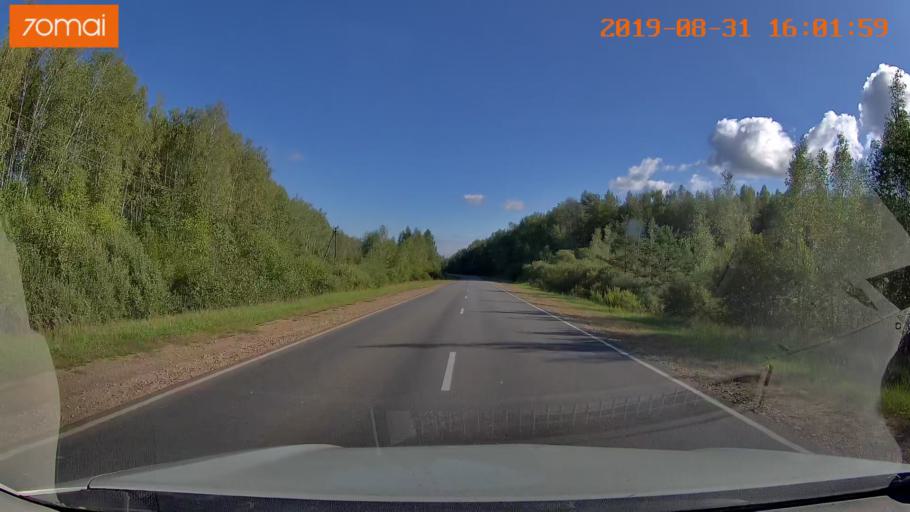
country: RU
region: Kaluga
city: Yukhnov
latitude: 54.6813
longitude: 35.2960
